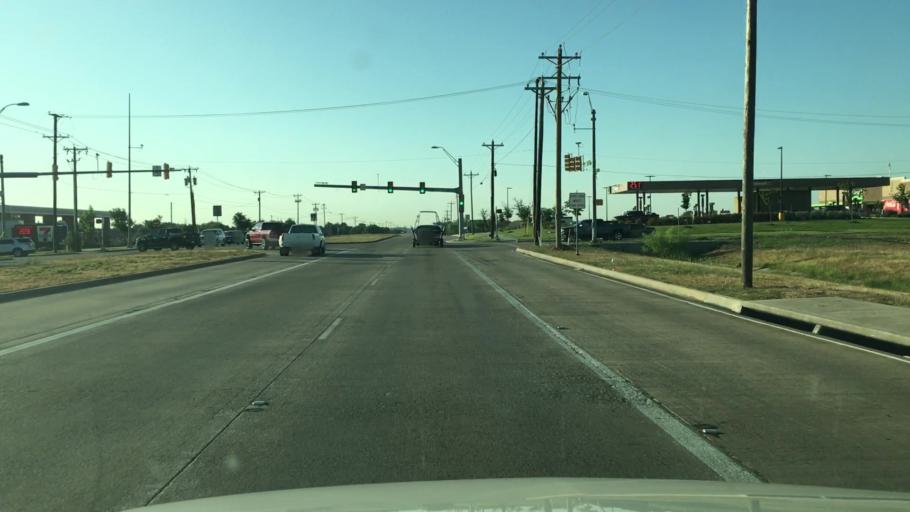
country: US
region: Texas
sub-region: Tarrant County
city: Crowley
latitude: 32.5397
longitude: -97.3618
